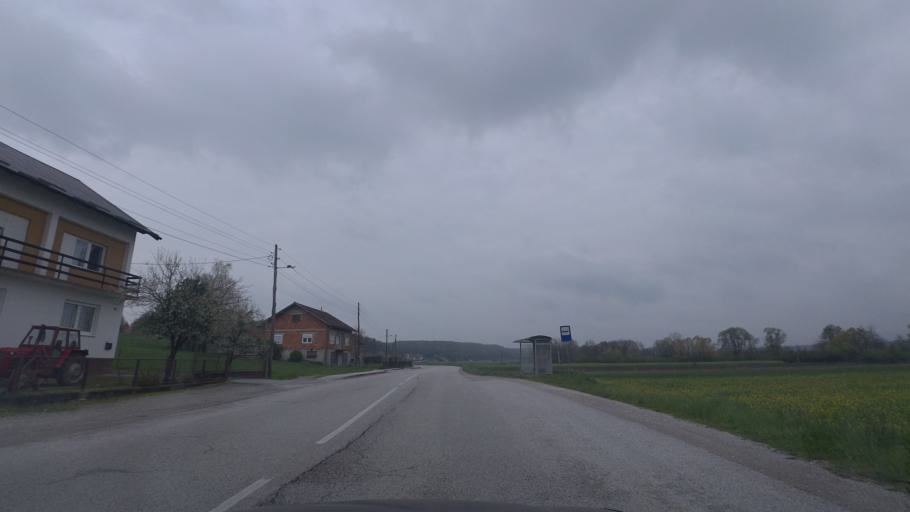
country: HR
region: Zagrebacka
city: Jastrebarsko
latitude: 45.6200
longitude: 15.5714
